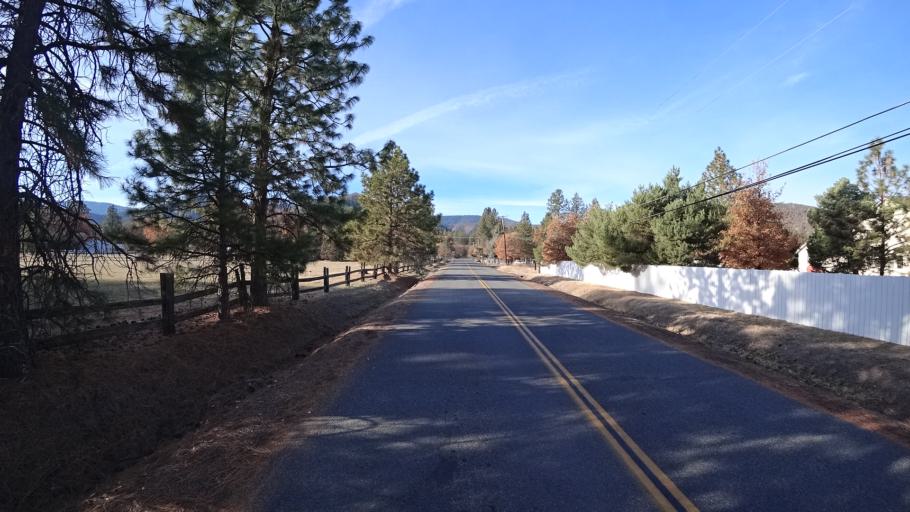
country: US
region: California
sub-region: Siskiyou County
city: Yreka
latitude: 41.6779
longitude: -122.6338
